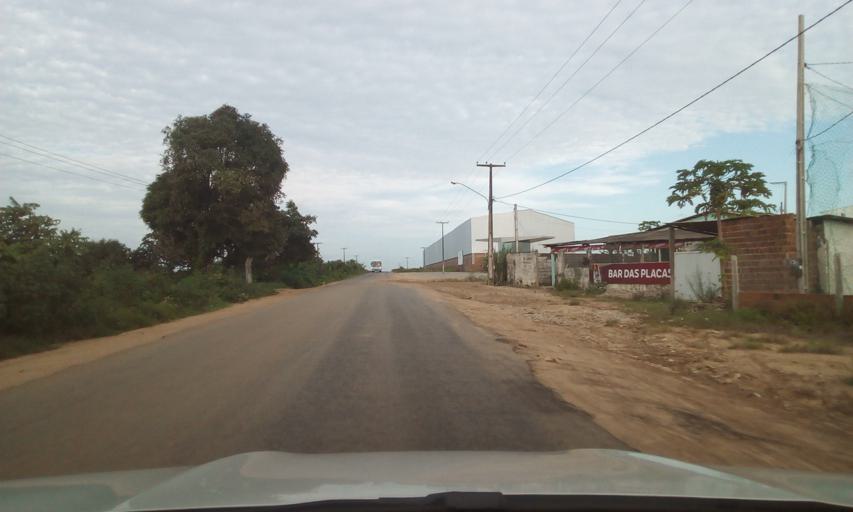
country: BR
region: Paraiba
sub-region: Conde
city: Conde
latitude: -7.2710
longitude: -34.8747
